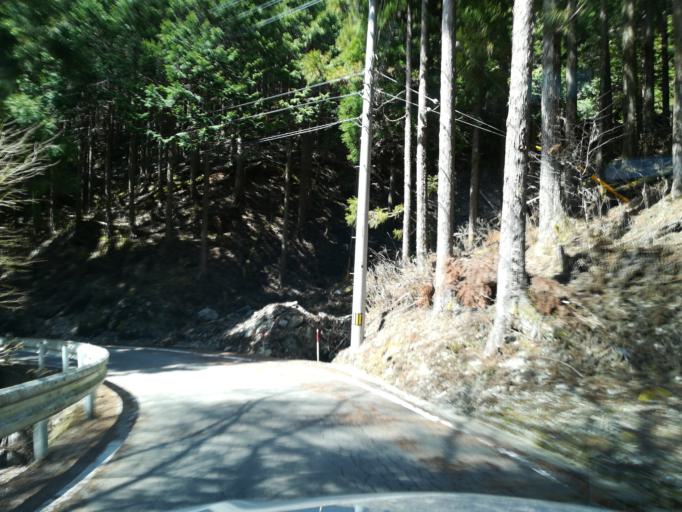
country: JP
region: Tokushima
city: Wakimachi
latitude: 33.8582
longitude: 134.0559
